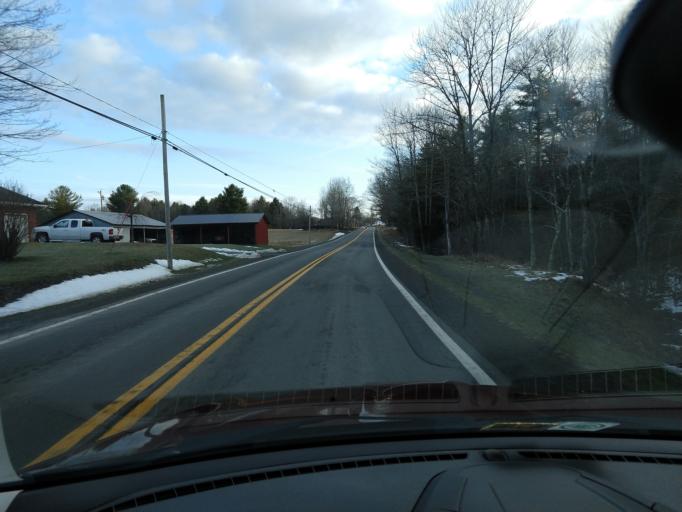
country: US
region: West Virginia
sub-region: Pocahontas County
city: Marlinton
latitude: 38.0744
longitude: -80.2868
